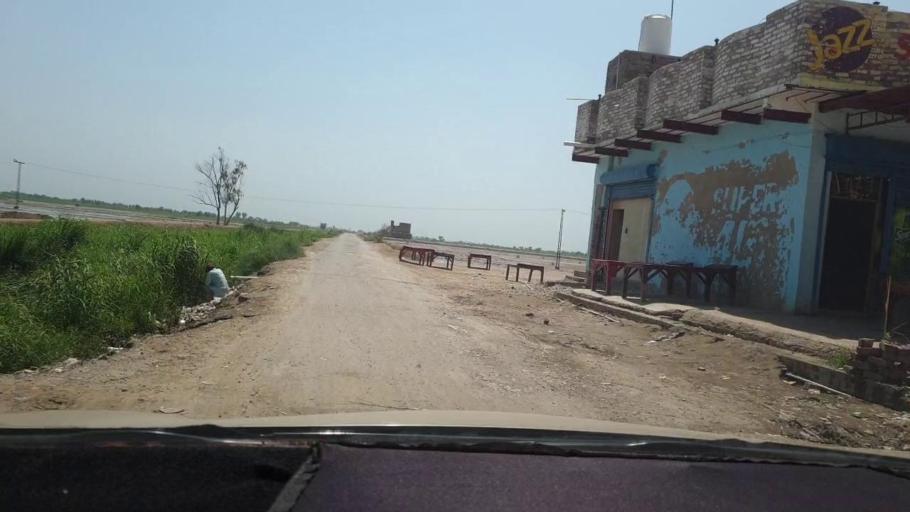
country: PK
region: Sindh
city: Shahdadkot
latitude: 27.8489
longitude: 67.9482
